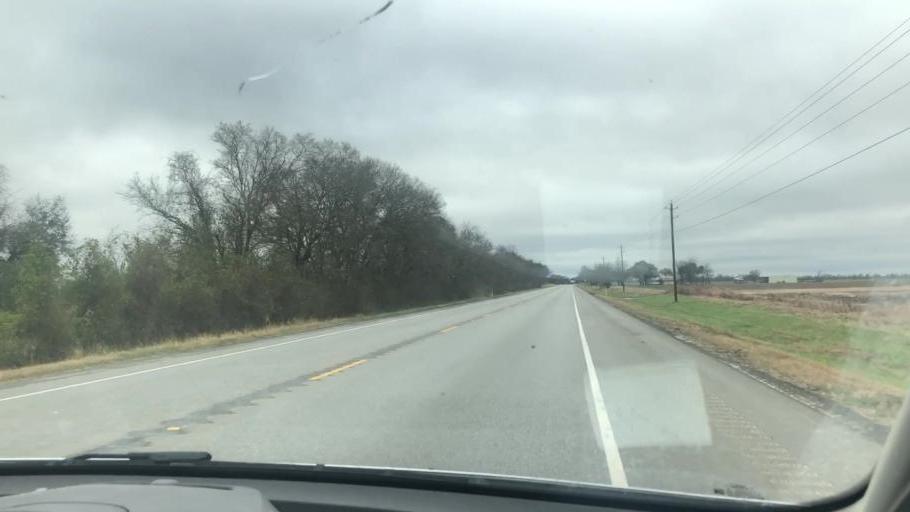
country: US
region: Texas
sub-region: Matagorda County
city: Bay City
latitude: 29.0728
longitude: -95.9720
